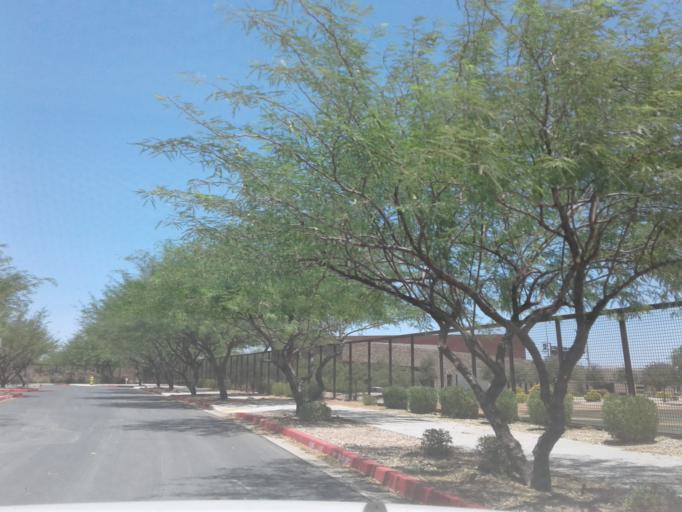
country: US
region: Arizona
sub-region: Maricopa County
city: Litchfield Park
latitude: 33.5120
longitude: -112.2974
